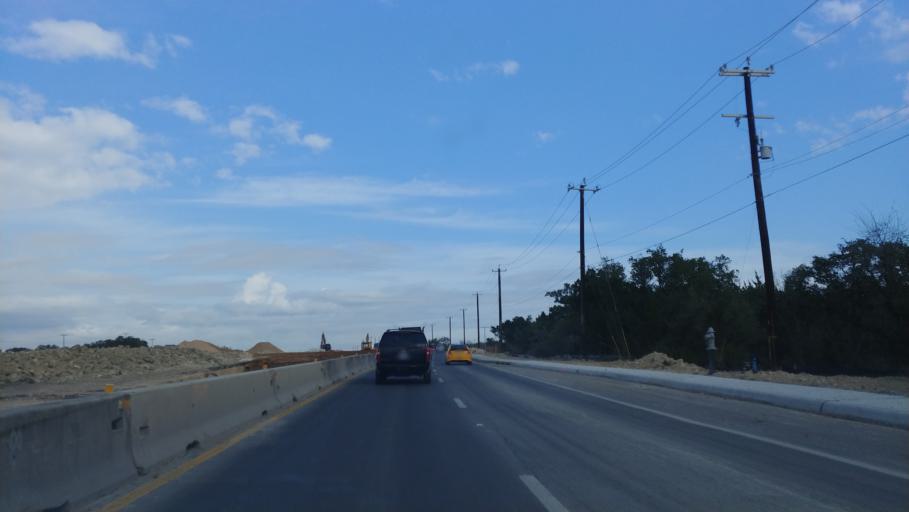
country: US
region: Texas
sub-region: Bexar County
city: Leon Valley
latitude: 29.4526
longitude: -98.7110
